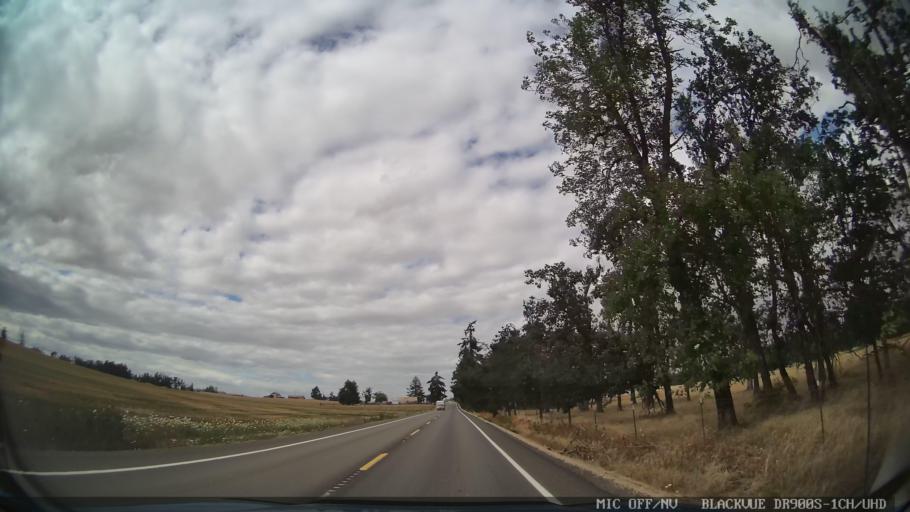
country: US
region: Oregon
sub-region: Marion County
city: Sublimity
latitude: 44.8562
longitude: -122.7930
